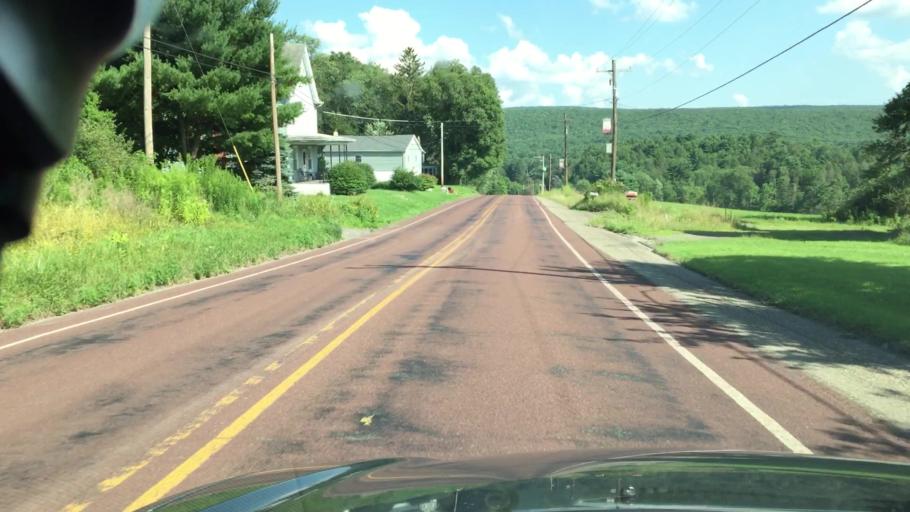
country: US
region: Pennsylvania
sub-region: Carbon County
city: Weatherly
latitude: 40.9223
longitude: -75.8628
